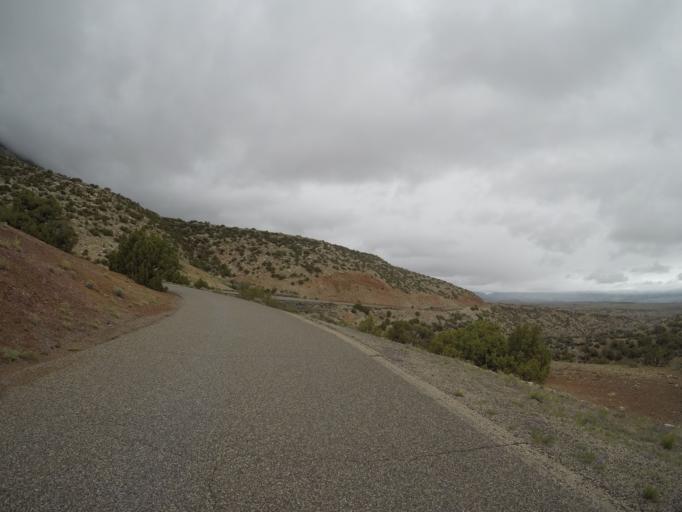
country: US
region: Wyoming
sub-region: Big Horn County
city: Lovell
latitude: 45.0362
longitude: -108.2569
